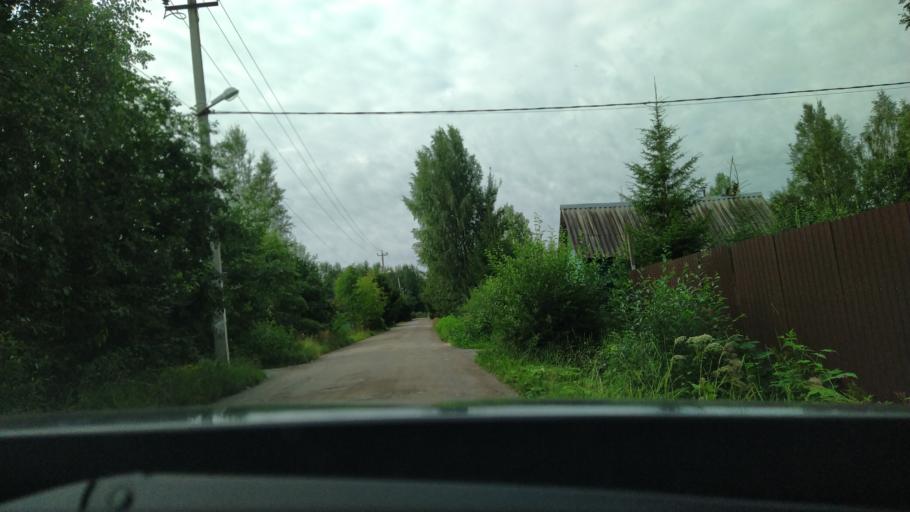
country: RU
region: Leningrad
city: Otradnoye
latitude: 59.7298
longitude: 30.8470
